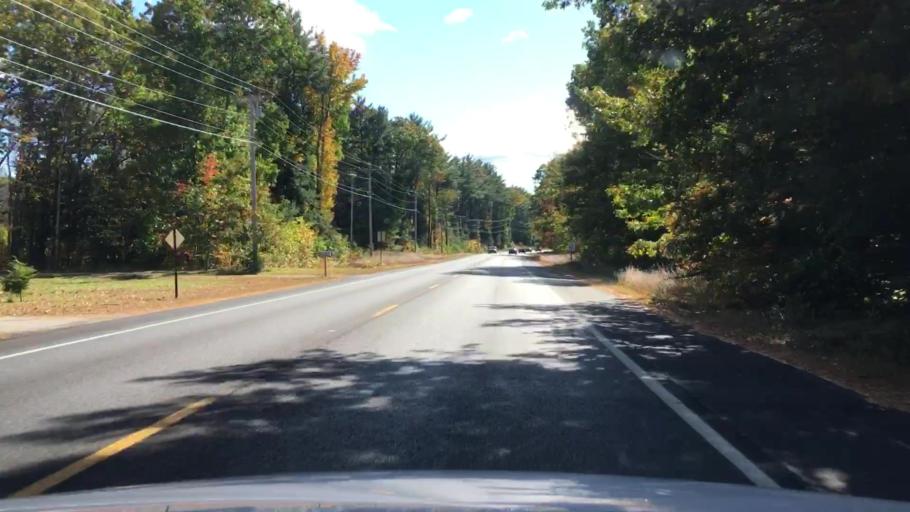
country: US
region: Maine
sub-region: York County
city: South Sanford
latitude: 43.4299
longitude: -70.7332
